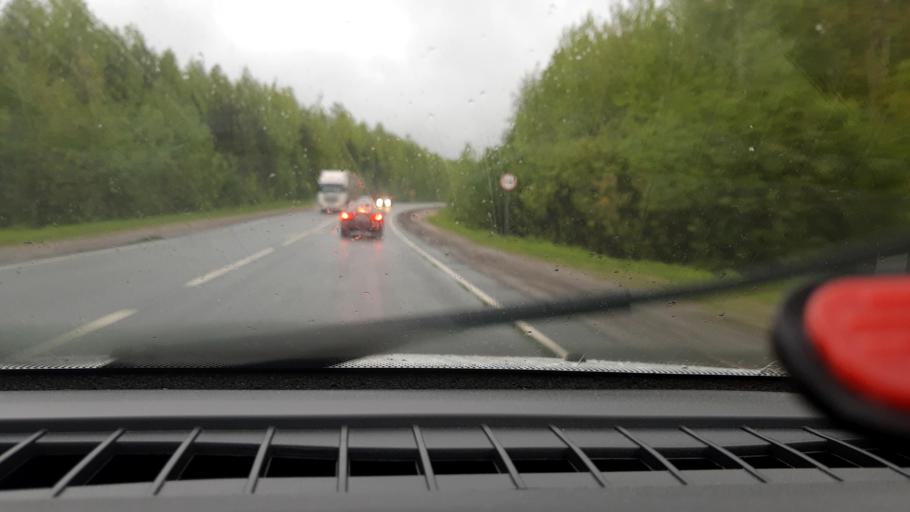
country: RU
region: Nizjnij Novgorod
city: Semenov
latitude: 56.7555
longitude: 44.3635
